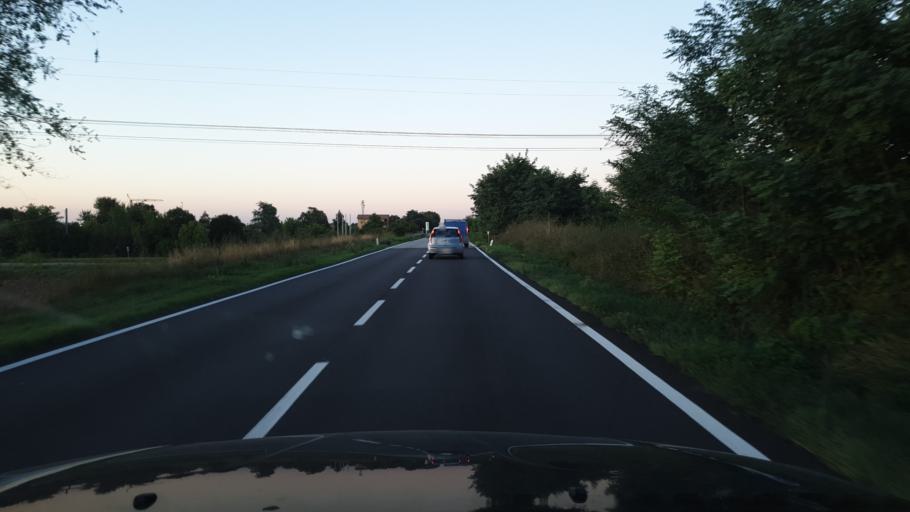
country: IT
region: Emilia-Romagna
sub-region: Provincia di Bologna
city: Ca De Fabbri
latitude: 44.6043
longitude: 11.4423
